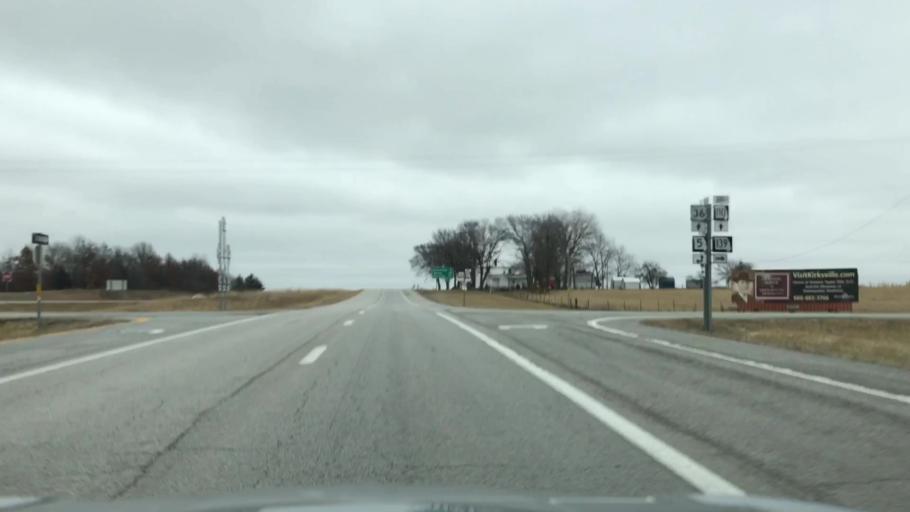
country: US
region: Missouri
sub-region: Linn County
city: Linneus
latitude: 39.7783
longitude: -93.1756
